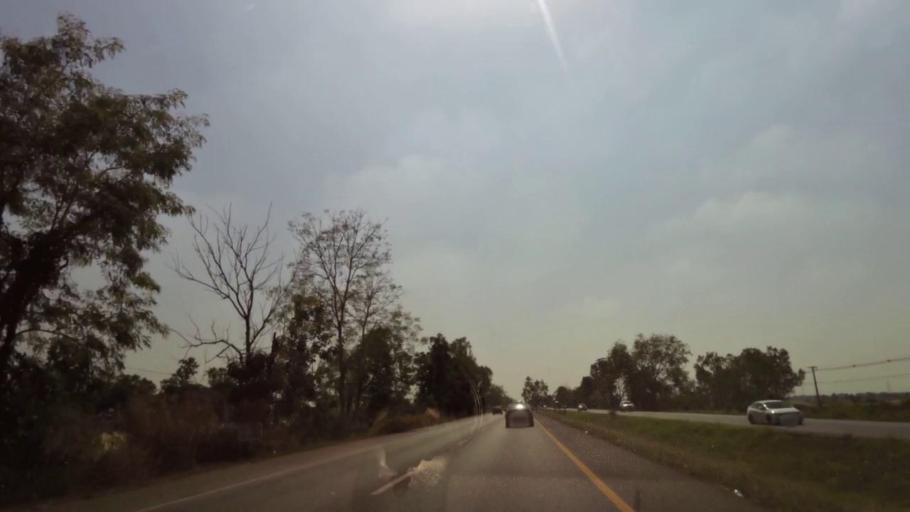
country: TH
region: Phichit
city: Wachira Barami
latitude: 16.4535
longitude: 100.1470
